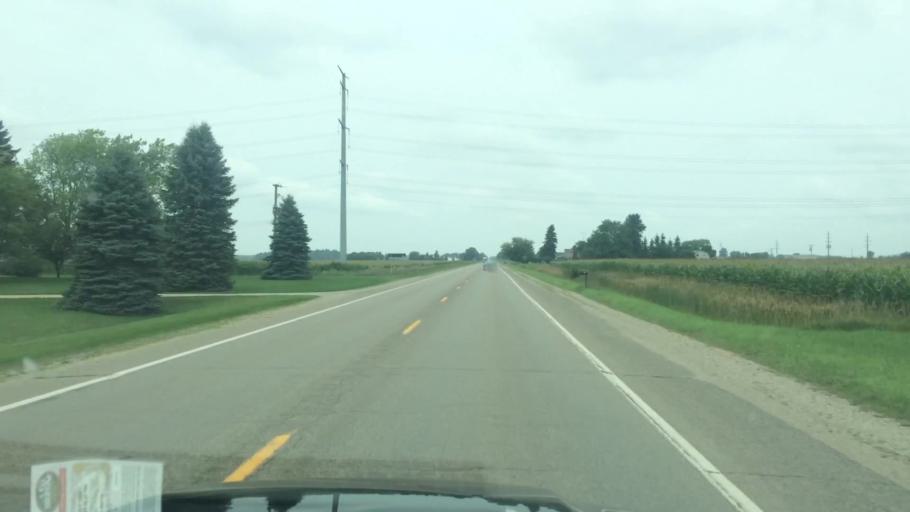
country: US
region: Michigan
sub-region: Huron County
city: Bad Axe
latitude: 43.8399
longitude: -83.0015
